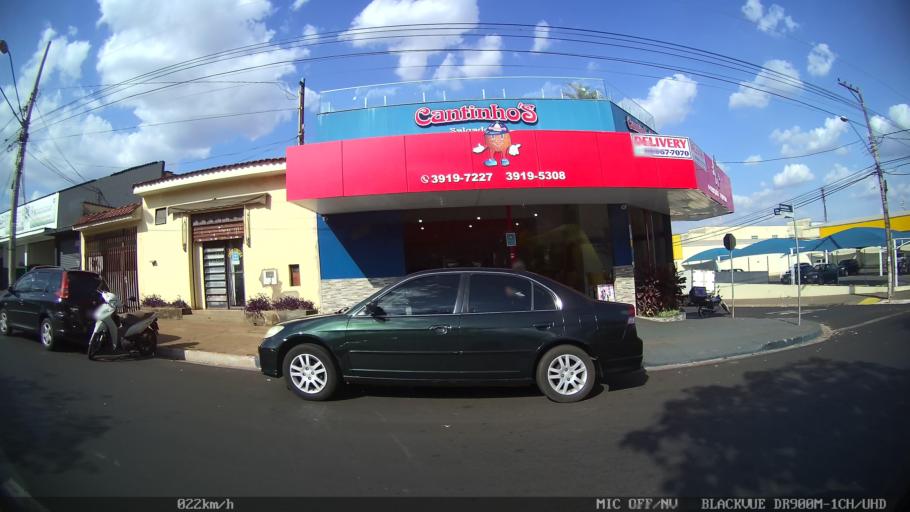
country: BR
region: Sao Paulo
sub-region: Ribeirao Preto
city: Ribeirao Preto
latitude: -21.1897
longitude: -47.8362
